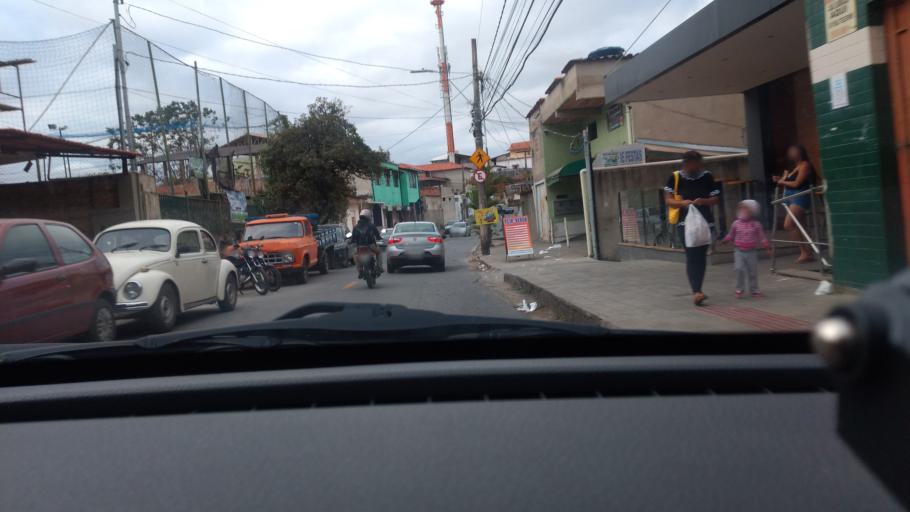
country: BR
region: Minas Gerais
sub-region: Santa Luzia
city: Santa Luzia
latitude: -19.8101
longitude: -43.9398
